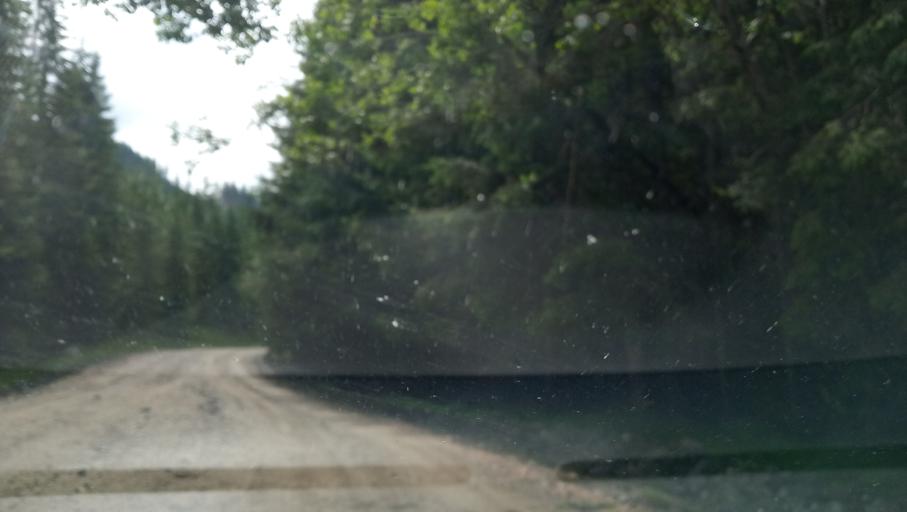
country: RO
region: Hunedoara
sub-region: Oras Petrila
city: Petrila
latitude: 45.4026
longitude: 23.5672
